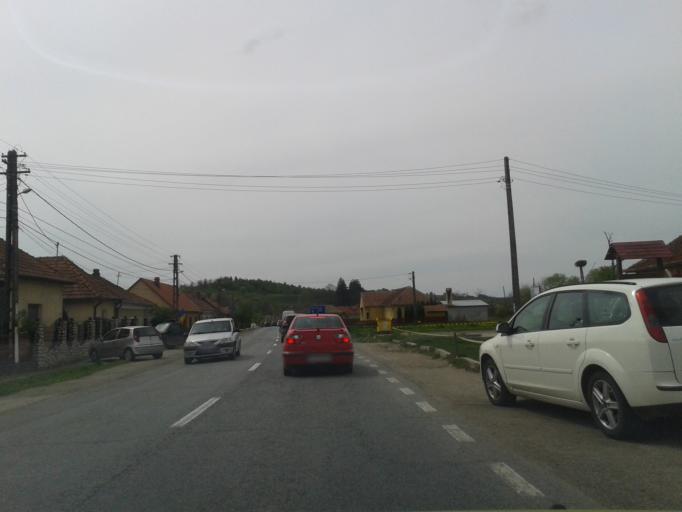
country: RO
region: Hunedoara
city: Lapugiu de Jos
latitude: 45.8875
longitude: 22.4519
